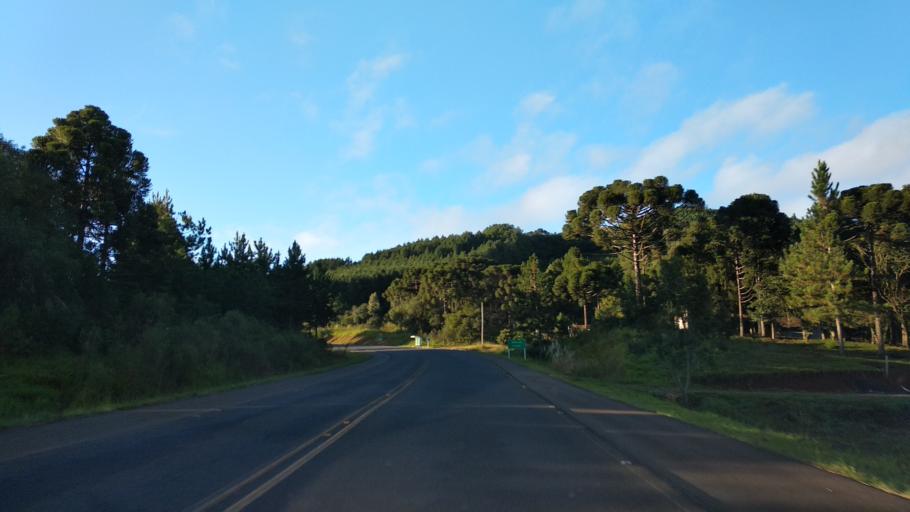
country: BR
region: Santa Catarina
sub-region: Curitibanos
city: Curitibanos
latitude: -27.6004
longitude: -50.7292
